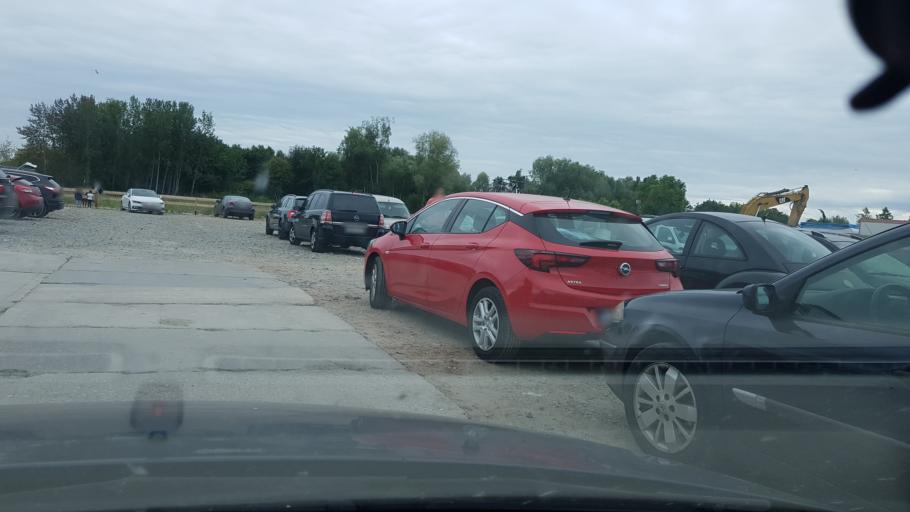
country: PL
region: Pomeranian Voivodeship
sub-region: Powiat nowodworski
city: Krynica Morska
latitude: 54.3786
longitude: 19.4423
